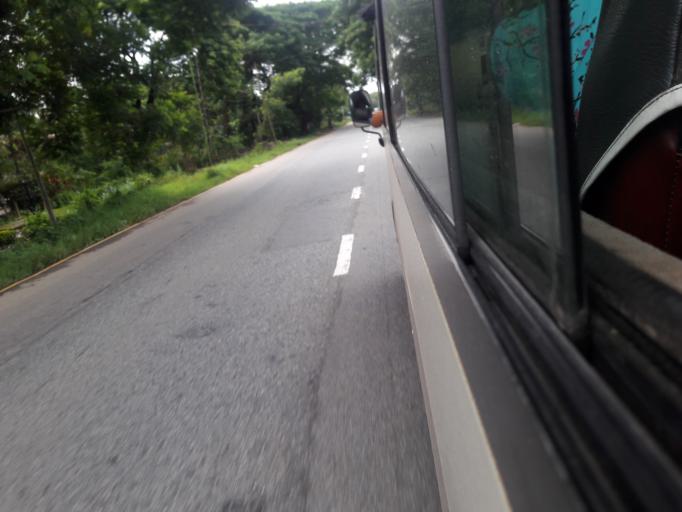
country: MM
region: Bago
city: Nyaunglebin
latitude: 17.8215
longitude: 96.6733
